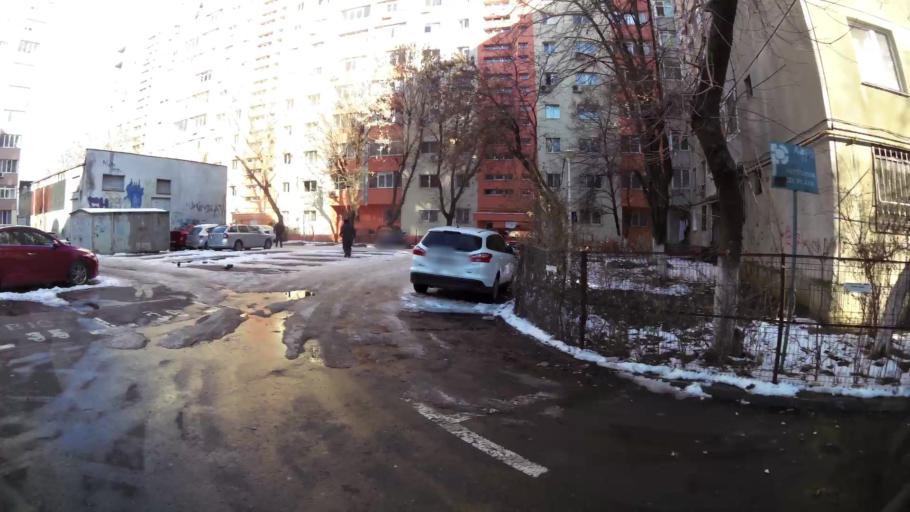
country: RO
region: Bucuresti
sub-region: Municipiul Bucuresti
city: Bucharest
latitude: 44.4599
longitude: 26.1247
